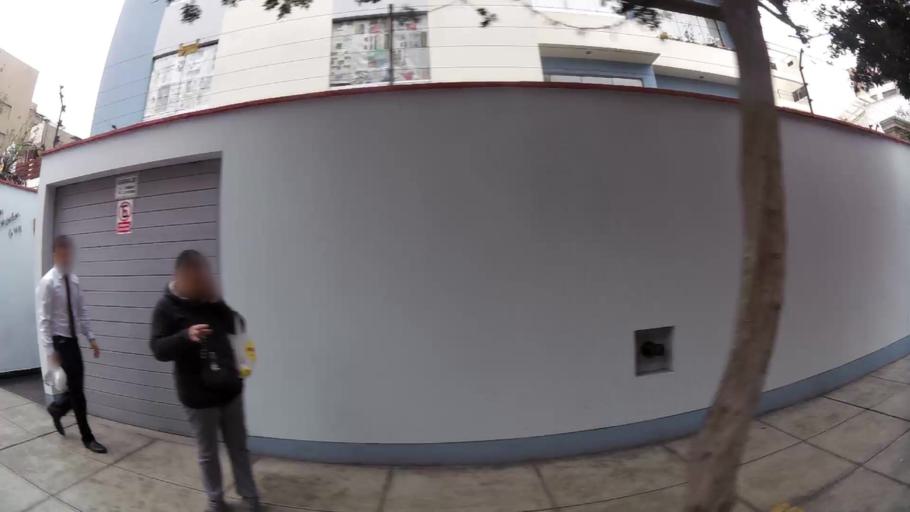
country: PE
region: Lima
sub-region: Lima
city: San Isidro
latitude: -12.1267
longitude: -77.0275
